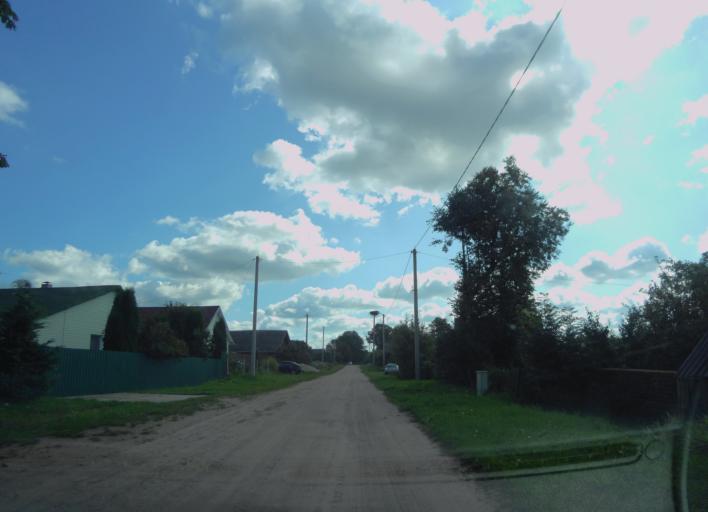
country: BY
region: Minsk
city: Zyembin
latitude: 54.3770
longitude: 28.3731
